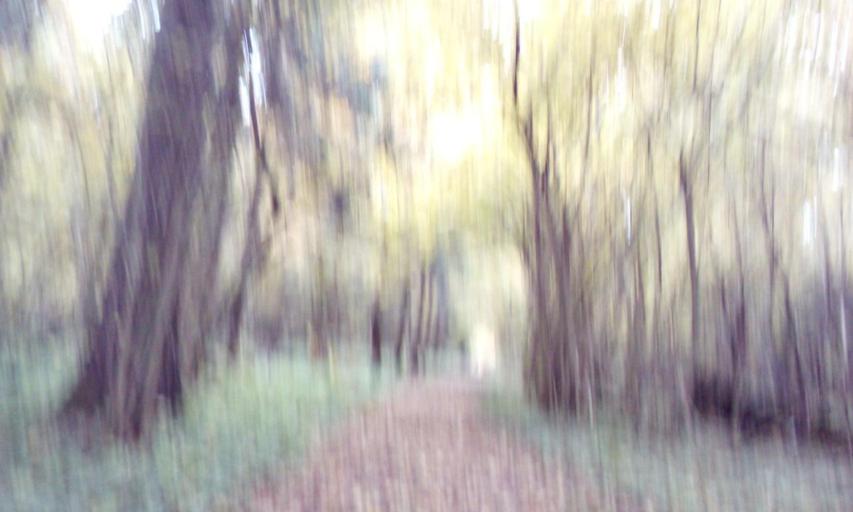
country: RU
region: Moskovskaya
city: Gorki Vtoryye
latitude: 55.6941
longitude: 37.1790
